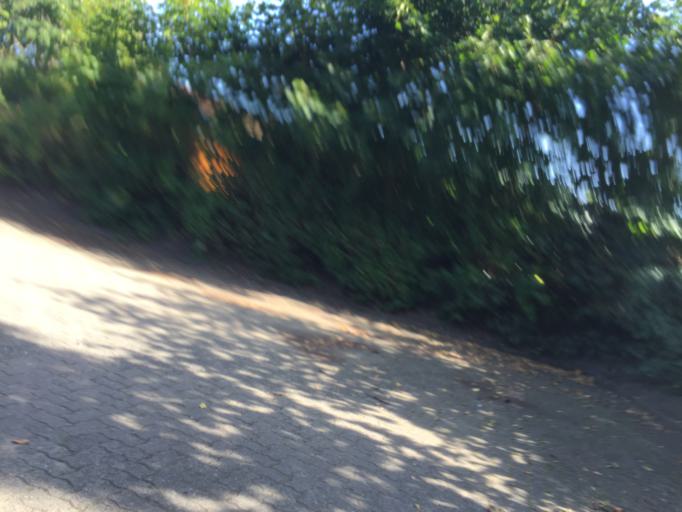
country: DE
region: Schleswig-Holstein
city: Itzehoe
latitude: 53.9092
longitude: 9.4990
